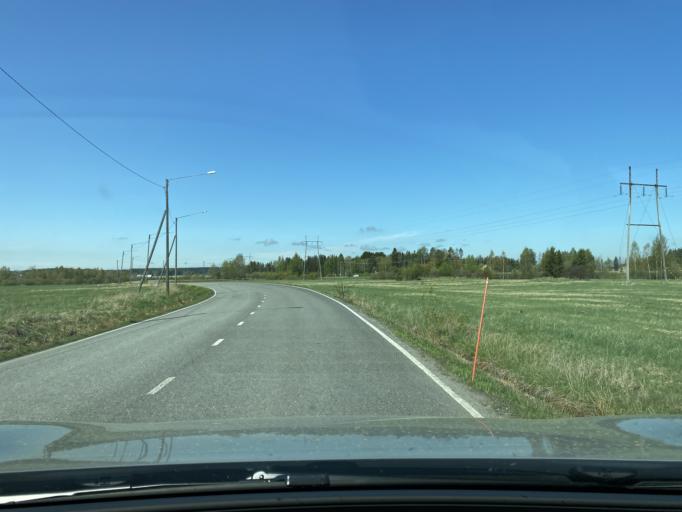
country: FI
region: Pirkanmaa
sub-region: Lounais-Pirkanmaa
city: Vammala
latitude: 61.3511
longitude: 22.8752
